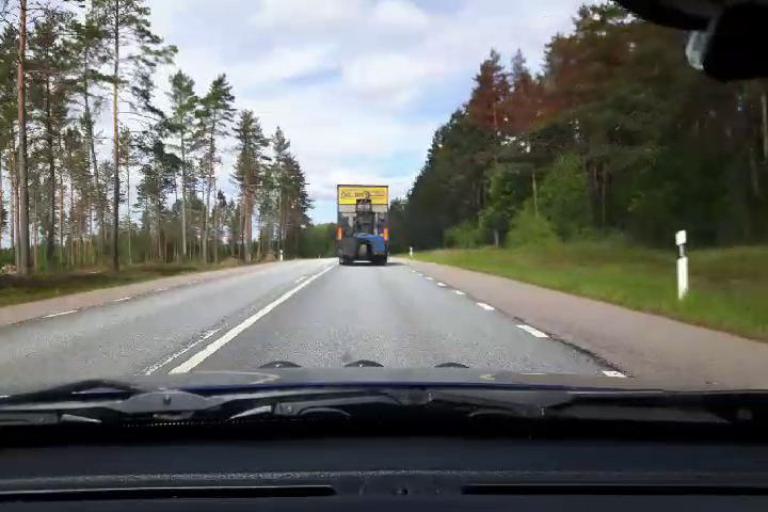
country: SE
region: Uppsala
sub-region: Tierps Kommun
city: Tierp
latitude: 60.2079
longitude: 17.4822
